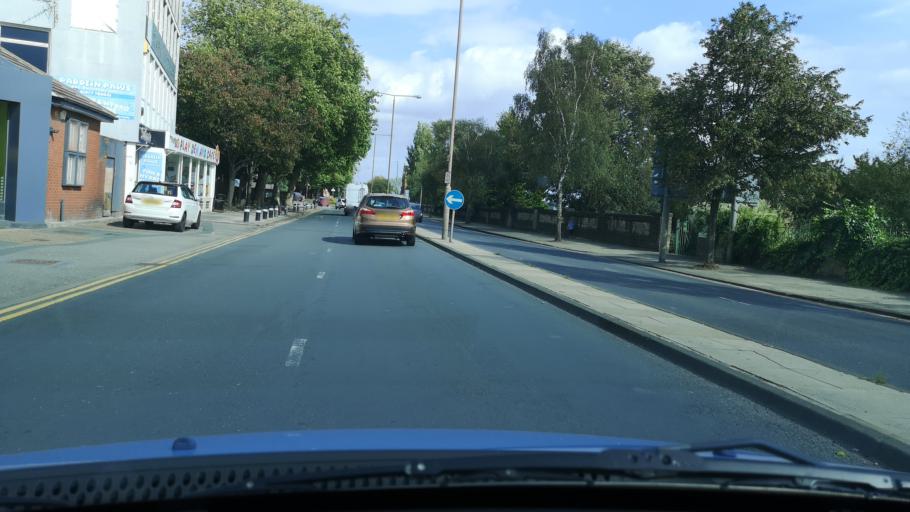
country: GB
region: England
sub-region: City and Borough of Wakefield
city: Pontefract
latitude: 53.6896
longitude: -1.3126
